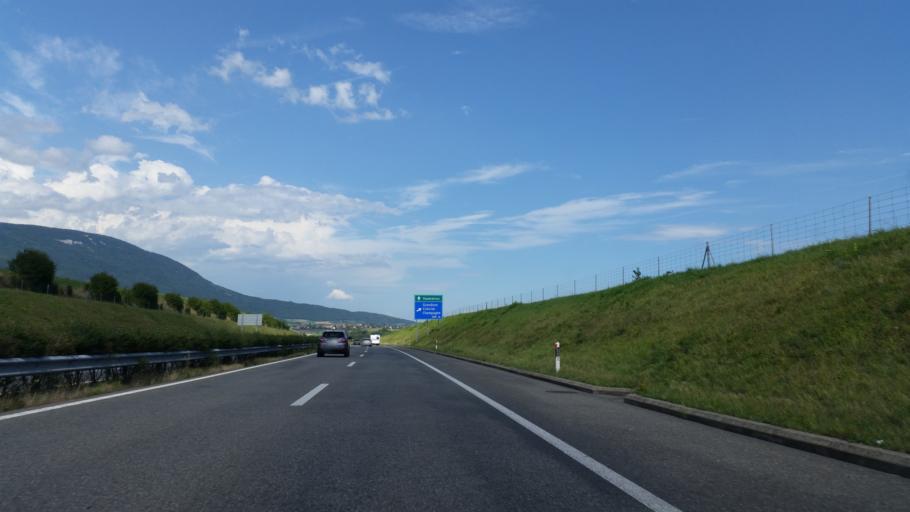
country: CH
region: Vaud
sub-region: Jura-Nord vaudois District
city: Grandson
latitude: 46.8159
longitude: 6.6493
